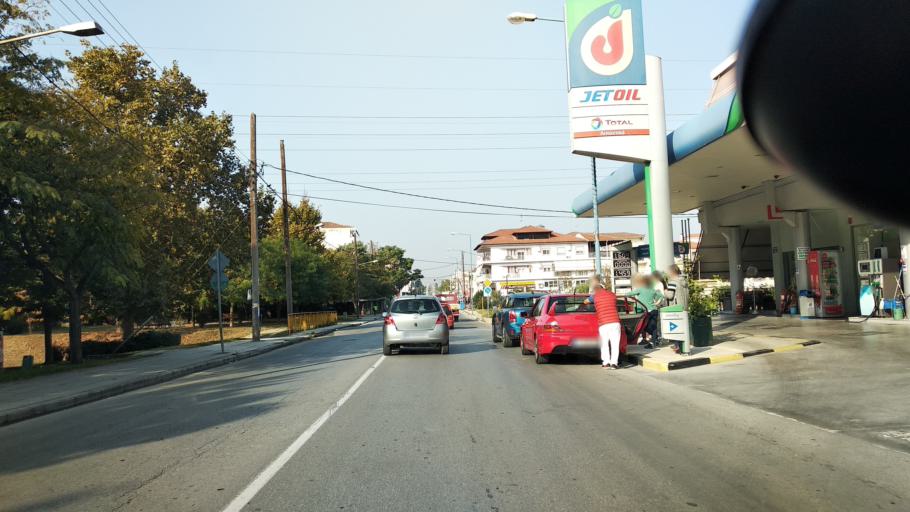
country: GR
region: Thessaly
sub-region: Nomos Larisis
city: Larisa
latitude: 39.6327
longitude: 22.3930
